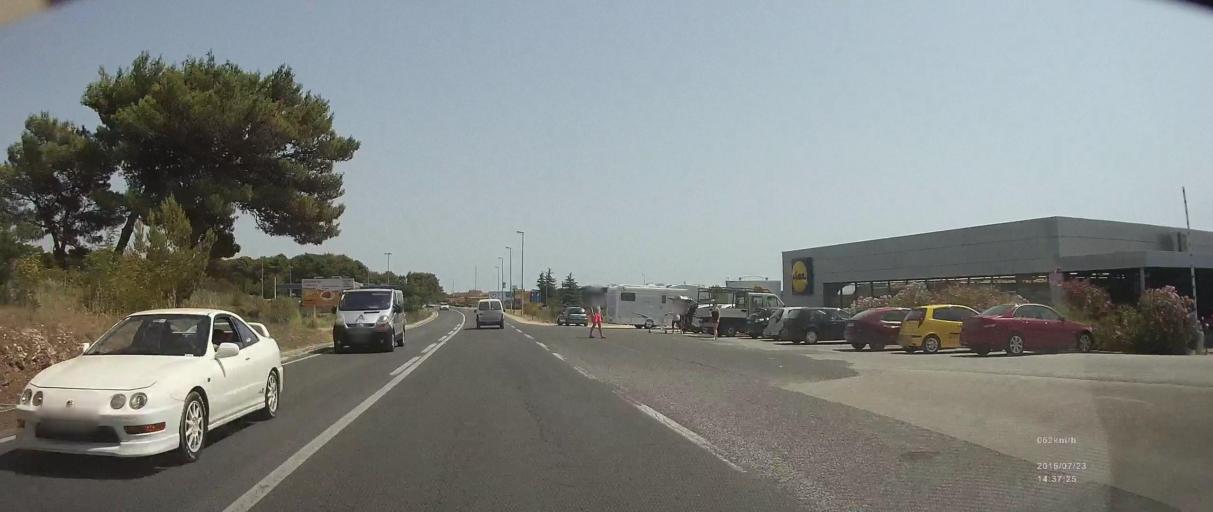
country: HR
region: Zadarska
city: Biograd na Moru
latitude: 43.9450
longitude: 15.4540
